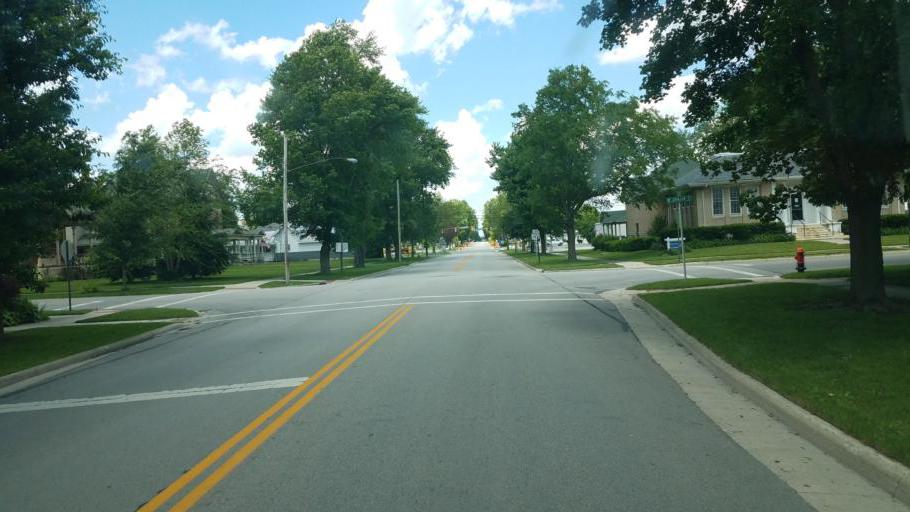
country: US
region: Ohio
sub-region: Wyandot County
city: Upper Sandusky
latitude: 40.8258
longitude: -83.2845
